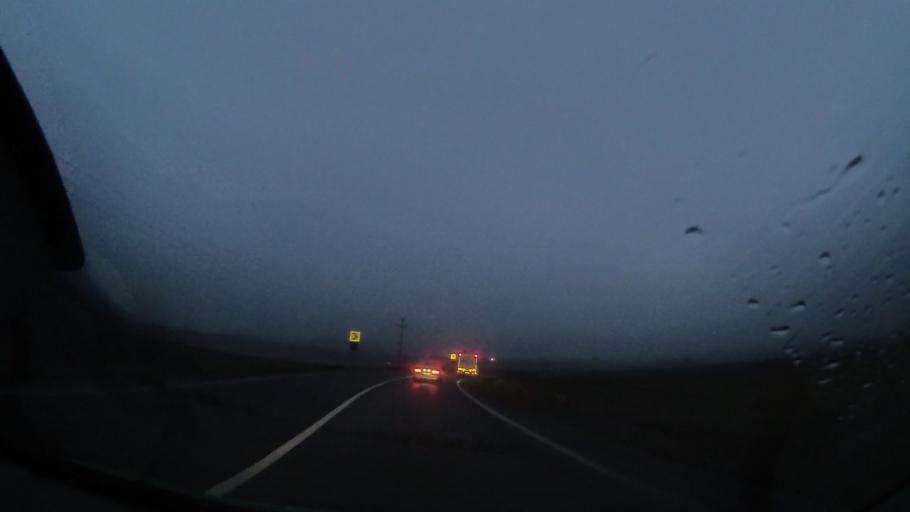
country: RO
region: Harghita
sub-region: Comuna Ditrau
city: Ditrau
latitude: 46.8224
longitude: 25.4922
